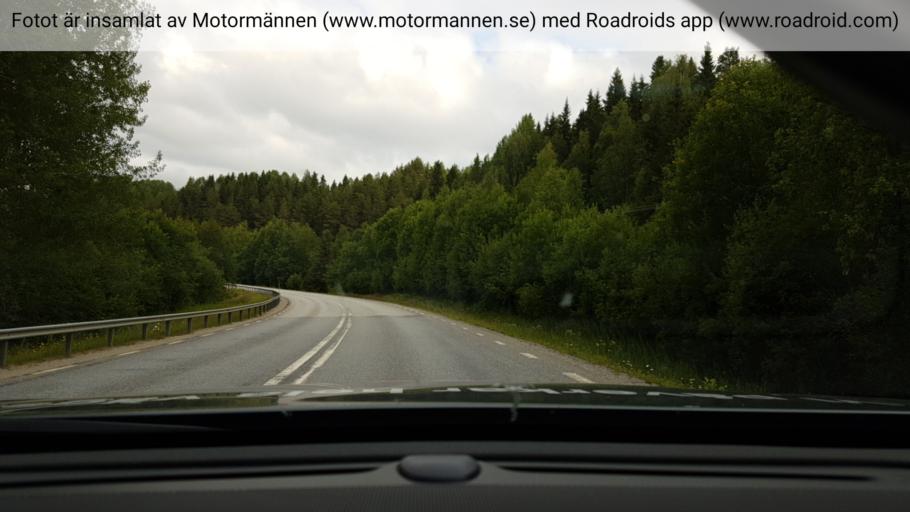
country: SE
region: Vaesterbotten
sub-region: Vindelns Kommun
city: Vindeln
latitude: 64.3108
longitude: 19.6078
